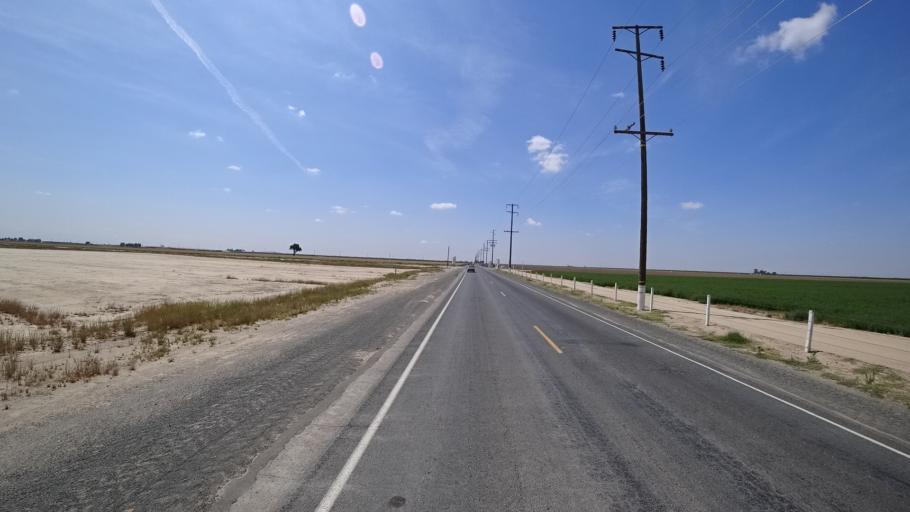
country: US
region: California
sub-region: Tulare County
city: Goshen
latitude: 36.2918
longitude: -119.4921
